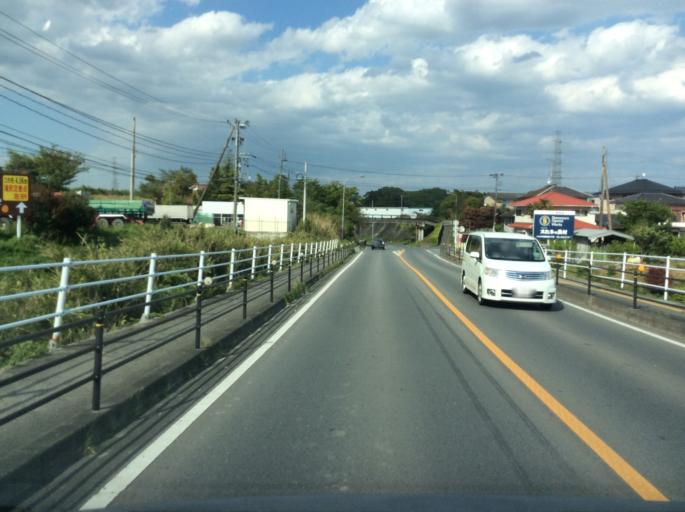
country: JP
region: Fukushima
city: Iwaki
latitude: 36.9304
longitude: 140.8265
